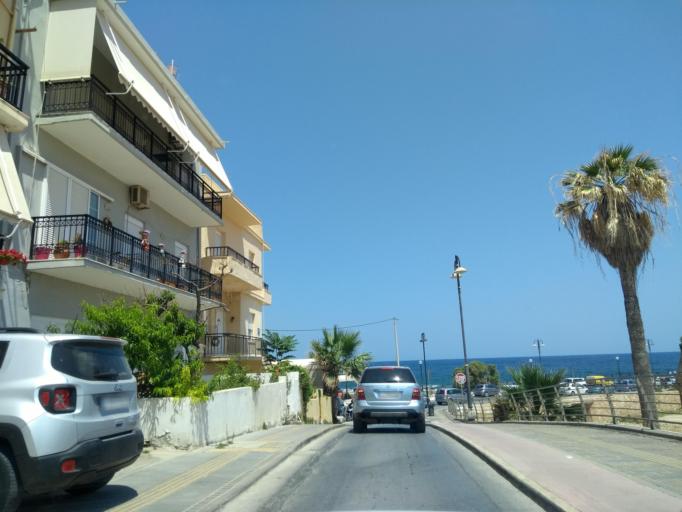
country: GR
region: Crete
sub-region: Nomos Chanias
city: Chania
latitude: 35.5176
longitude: 24.0137
